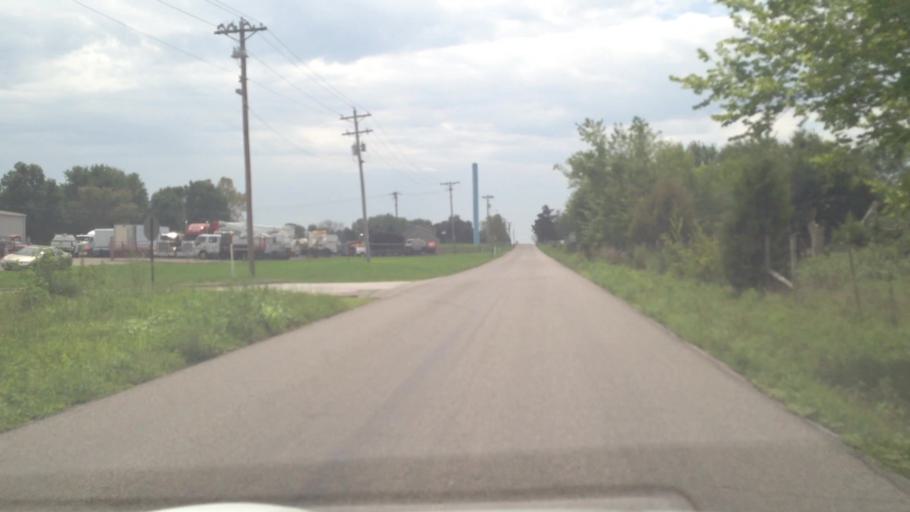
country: US
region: Kansas
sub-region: Crawford County
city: Girard
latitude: 37.5128
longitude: -94.8699
